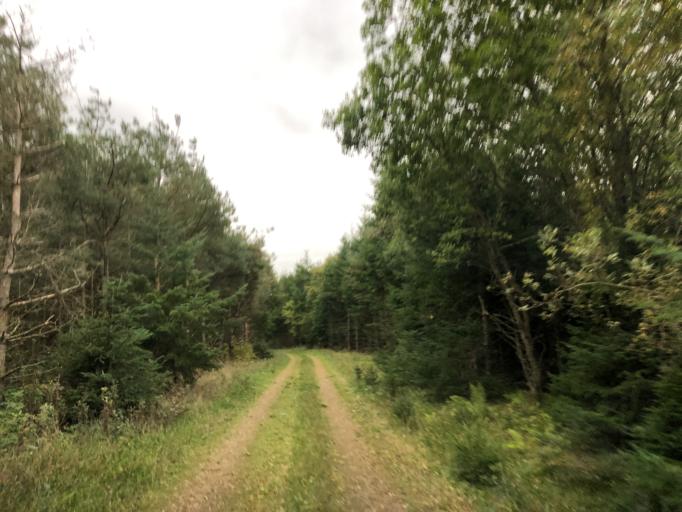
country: DK
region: Central Jutland
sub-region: Holstebro Kommune
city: Ulfborg
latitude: 56.2221
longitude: 8.4459
